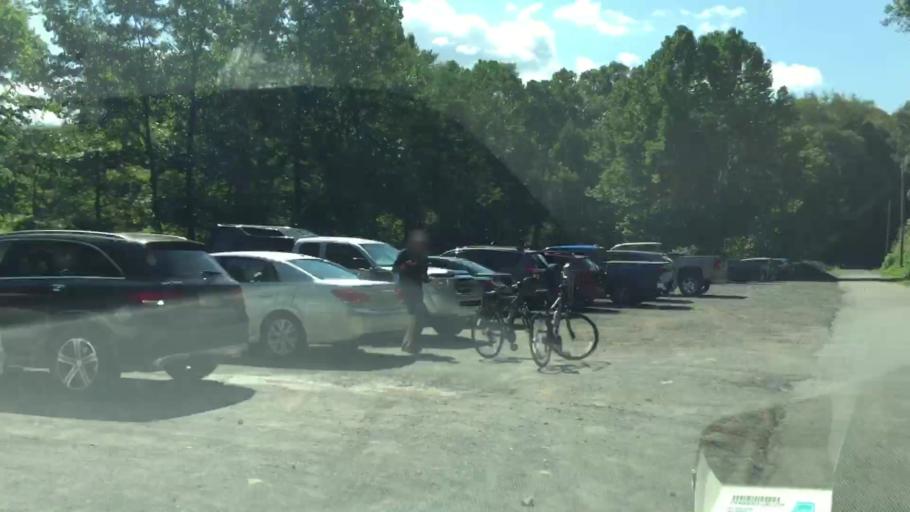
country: US
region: Pennsylvania
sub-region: Allegheny County
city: Coraopolis
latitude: 40.5042
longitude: -80.1451
